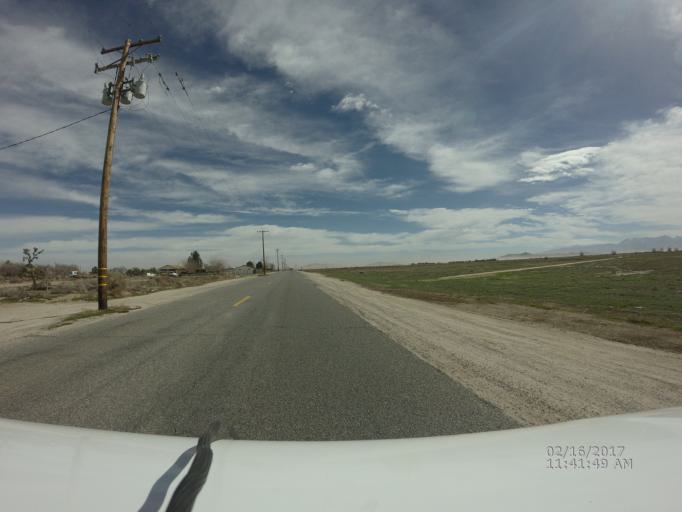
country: US
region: California
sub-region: Los Angeles County
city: Lake Los Angeles
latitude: 34.6903
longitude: -117.9683
